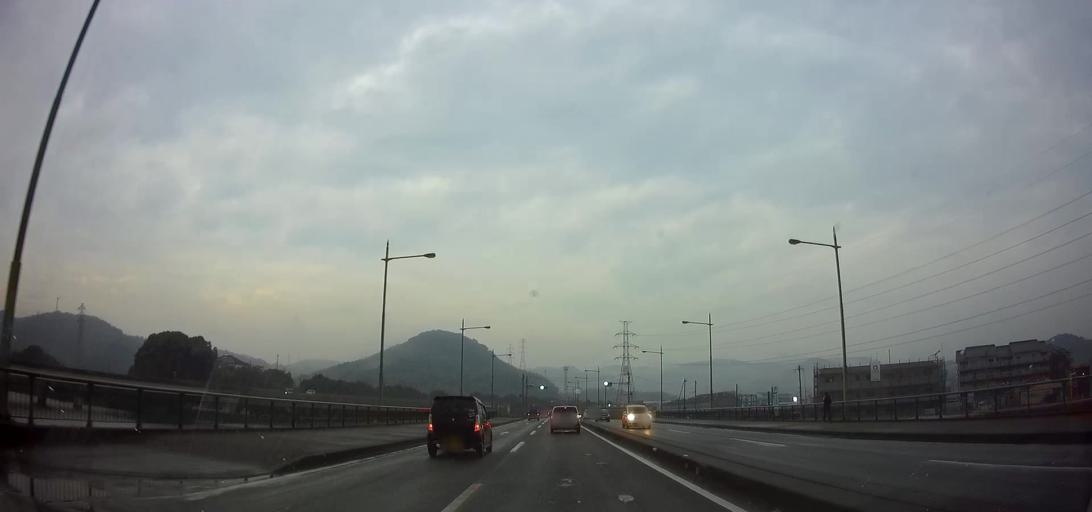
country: JP
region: Nagasaki
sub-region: Isahaya-shi
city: Isahaya
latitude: 32.8467
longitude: 130.0112
